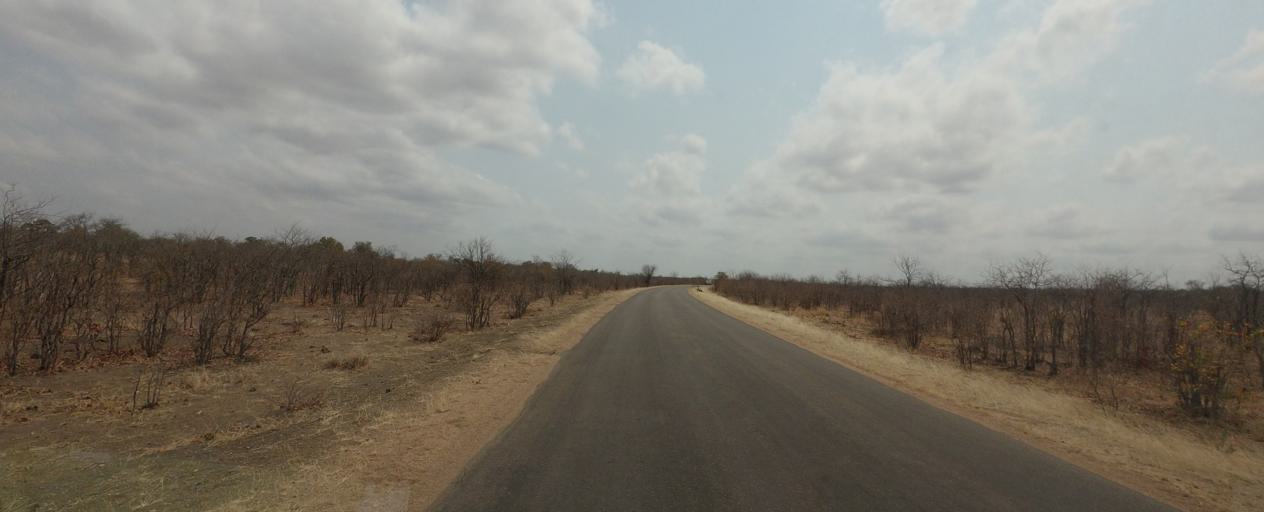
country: ZA
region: Limpopo
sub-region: Mopani District Municipality
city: Phalaborwa
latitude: -23.6060
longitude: 31.4546
